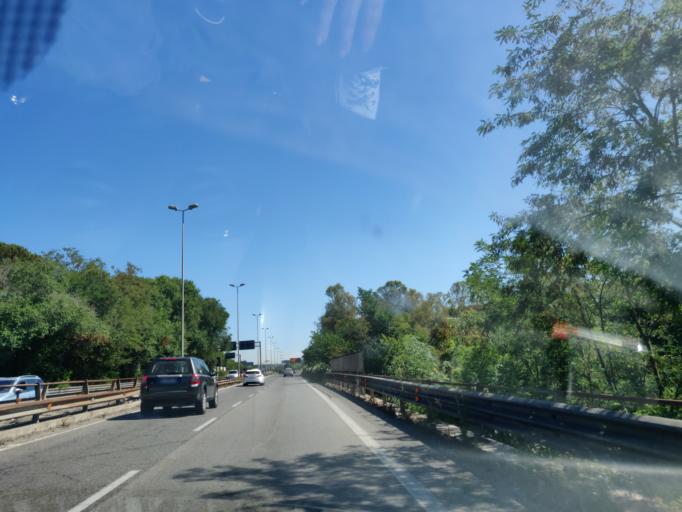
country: IT
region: Latium
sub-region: Citta metropolitana di Roma Capitale
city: Selcetta
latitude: 41.8107
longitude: 12.4587
